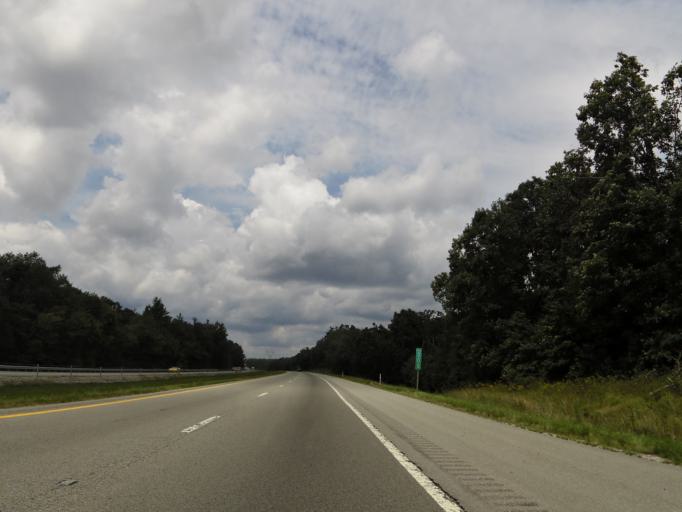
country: US
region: Tennessee
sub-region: Putnam County
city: Monterey
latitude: 36.0677
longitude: -85.1897
